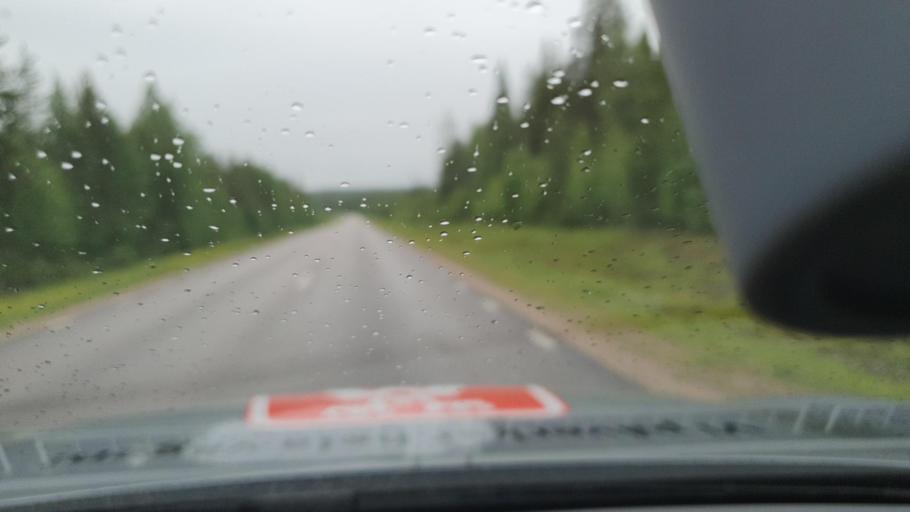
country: SE
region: Norrbotten
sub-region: Overtornea Kommun
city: OEvertornea
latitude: 66.4100
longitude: 23.4477
